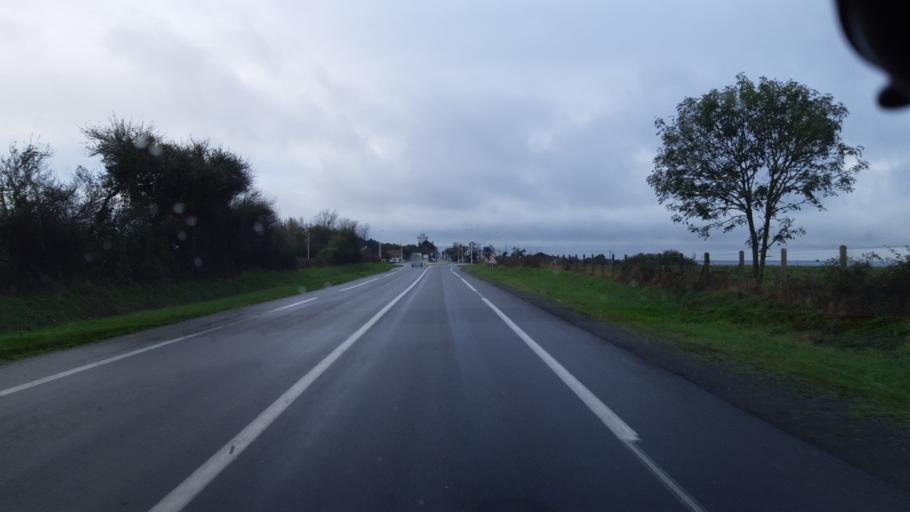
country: FR
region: Lower Normandy
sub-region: Departement de la Manche
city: Donville-les-Bains
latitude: 48.8599
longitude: -1.5527
